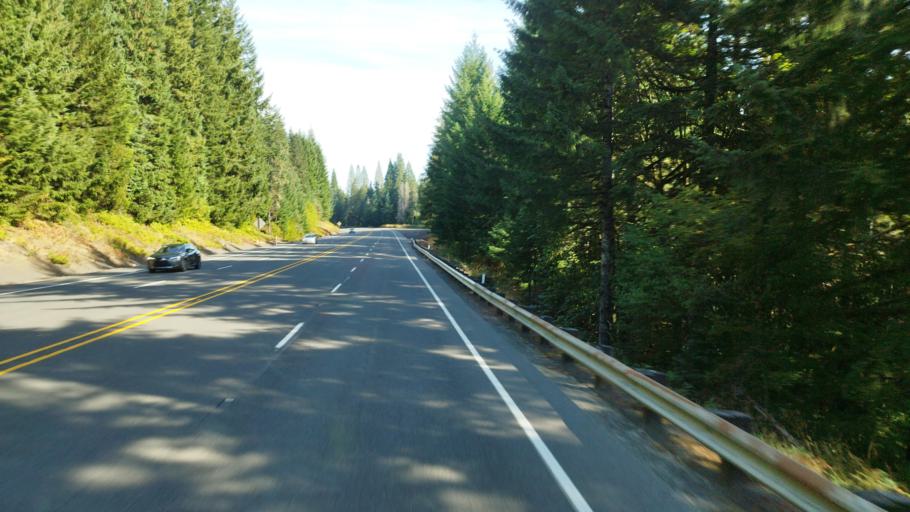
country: US
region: Oregon
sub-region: Columbia County
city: Vernonia
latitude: 45.7737
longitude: -123.3731
